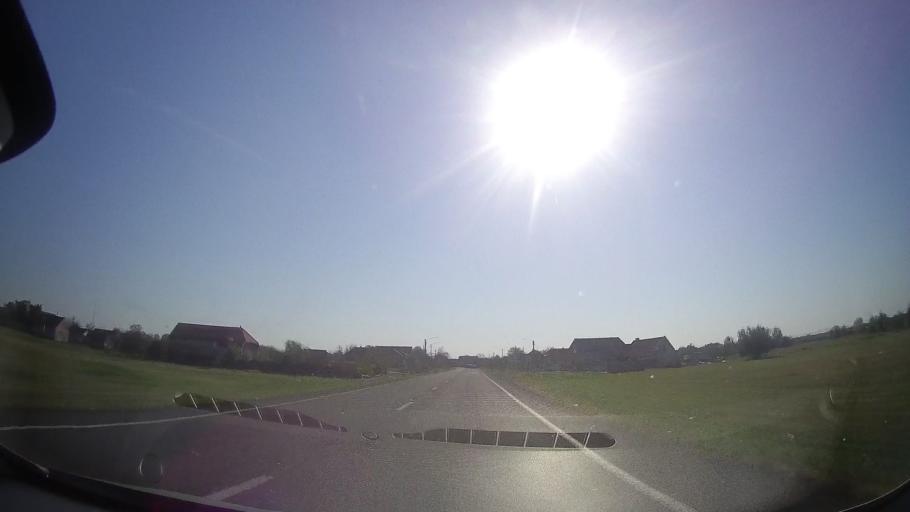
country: RO
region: Timis
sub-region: Comuna Topolovatu Mare
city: Topolovatu Mare
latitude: 45.7781
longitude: 21.6108
